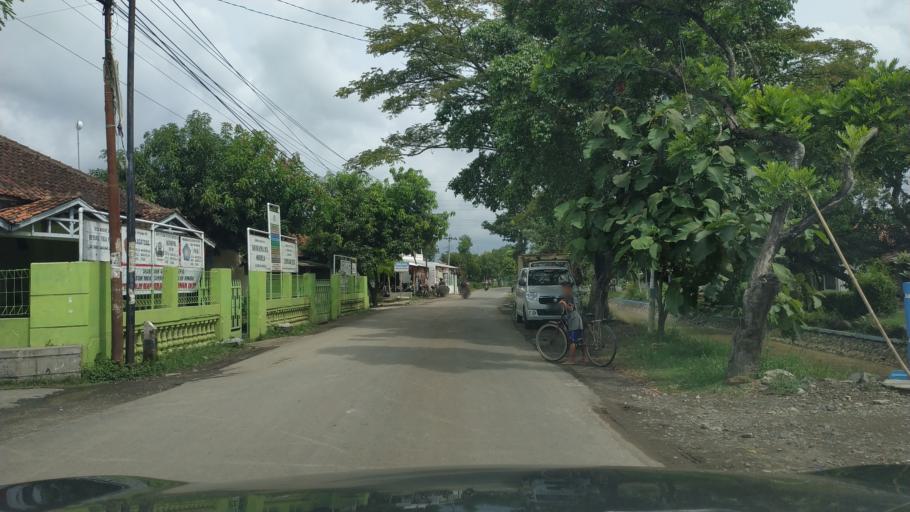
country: ID
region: Central Java
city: Pemalang
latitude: -6.9141
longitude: 109.3291
